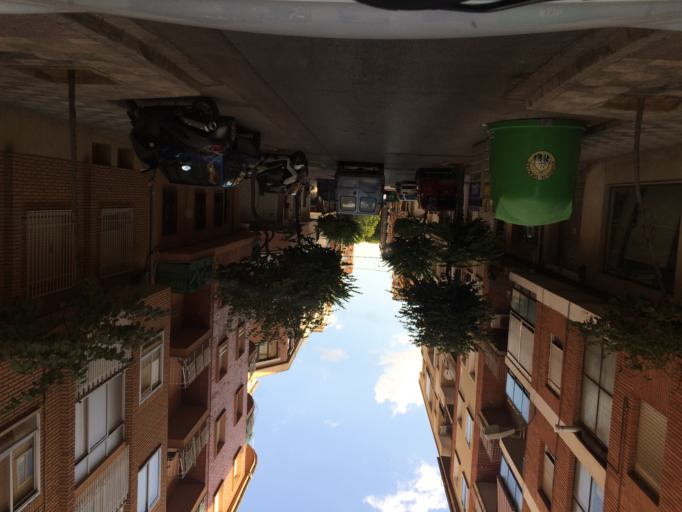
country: ES
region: Castille-La Mancha
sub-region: Provincia de Albacete
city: Albacete
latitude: 38.9943
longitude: -1.8656
